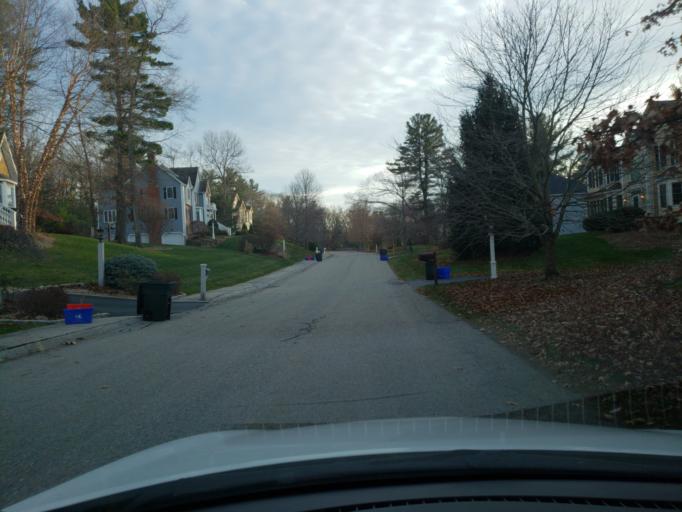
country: US
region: Massachusetts
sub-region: Essex County
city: Lawrence
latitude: 42.6764
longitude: -71.1919
